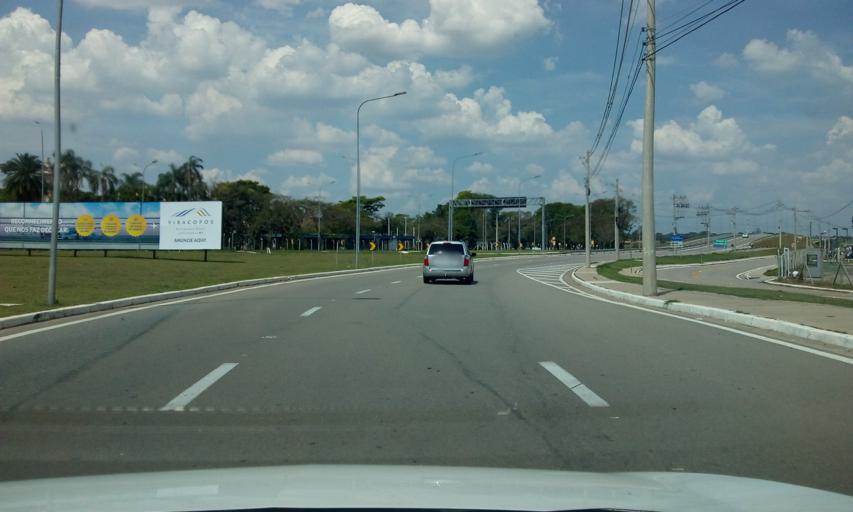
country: BR
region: Sao Paulo
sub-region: Indaiatuba
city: Indaiatuba
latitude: -23.0126
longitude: -47.1441
